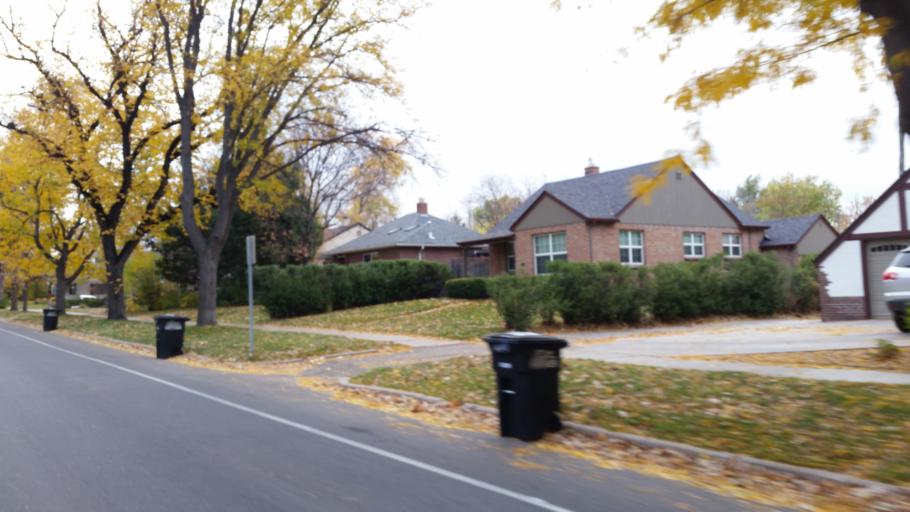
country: US
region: Colorado
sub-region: Arapahoe County
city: Glendale
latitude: 39.7434
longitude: -104.9334
